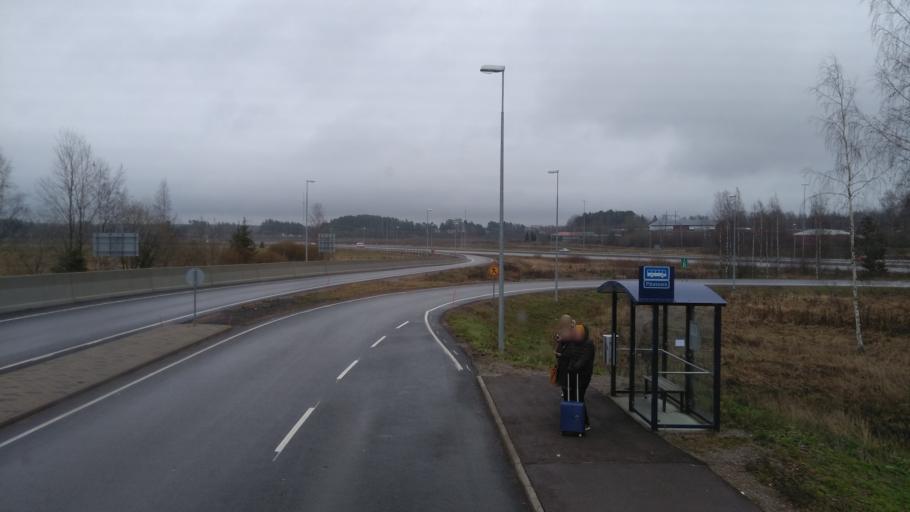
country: FI
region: Uusimaa
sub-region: Loviisa
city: Lovisa
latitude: 60.4620
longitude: 26.1930
